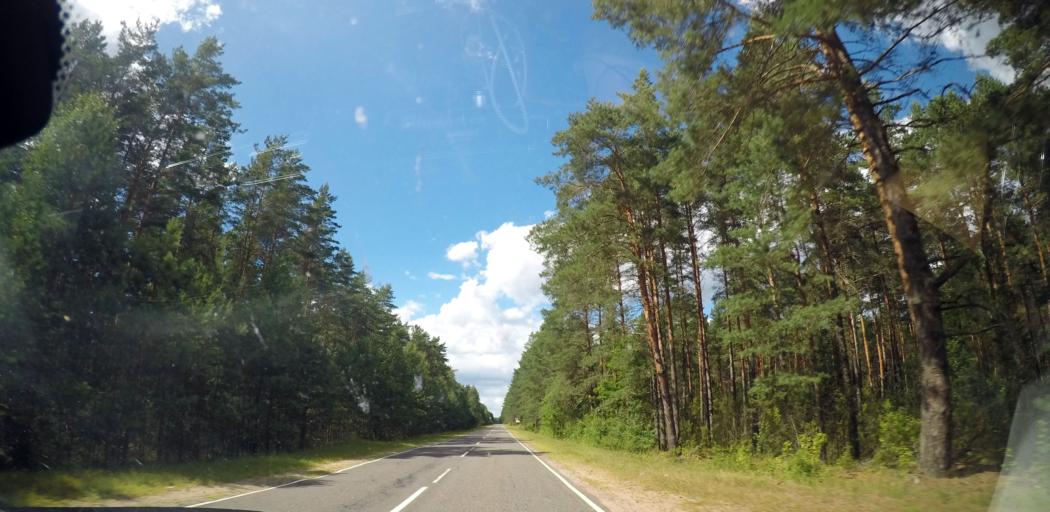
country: LT
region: Alytaus apskritis
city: Druskininkai
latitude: 53.8620
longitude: 24.1760
